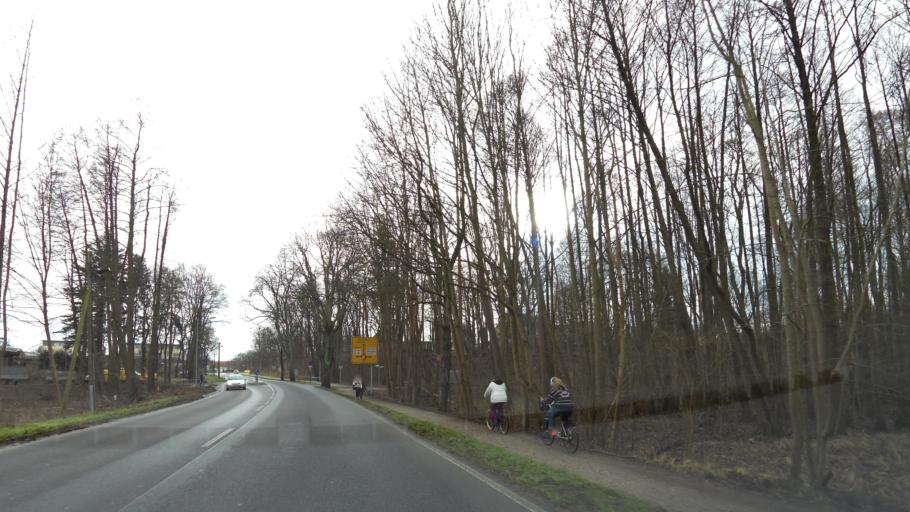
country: DE
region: Brandenburg
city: Strausberg
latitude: 52.5899
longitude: 13.8932
